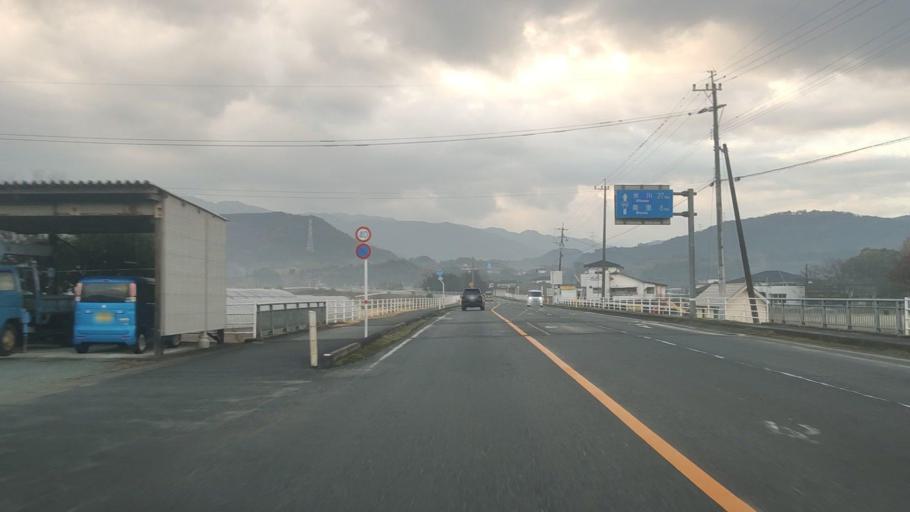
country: JP
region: Kumamoto
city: Matsubase
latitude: 32.6476
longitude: 130.8115
